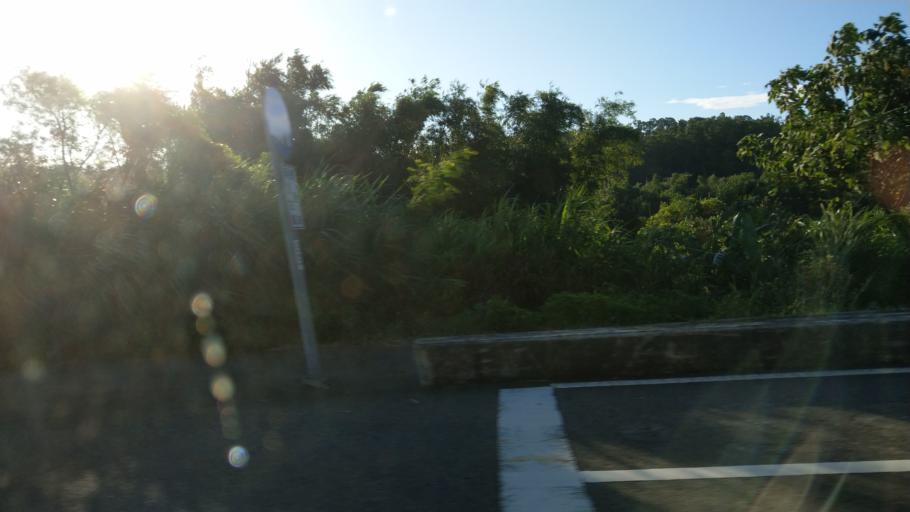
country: TW
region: Taiwan
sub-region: Miaoli
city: Miaoli
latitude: 24.5411
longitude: 120.7969
